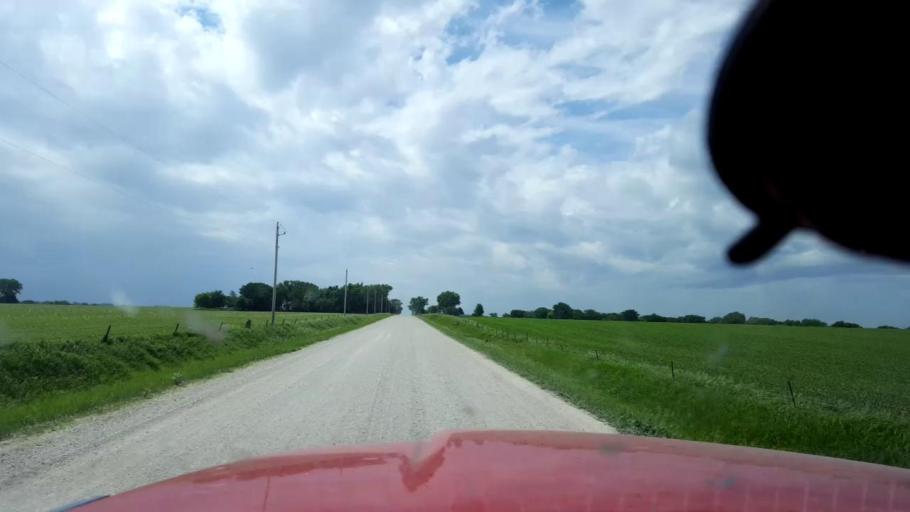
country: US
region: Iowa
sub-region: Cherokee County
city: Cherokee
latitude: 42.8138
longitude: -95.5345
